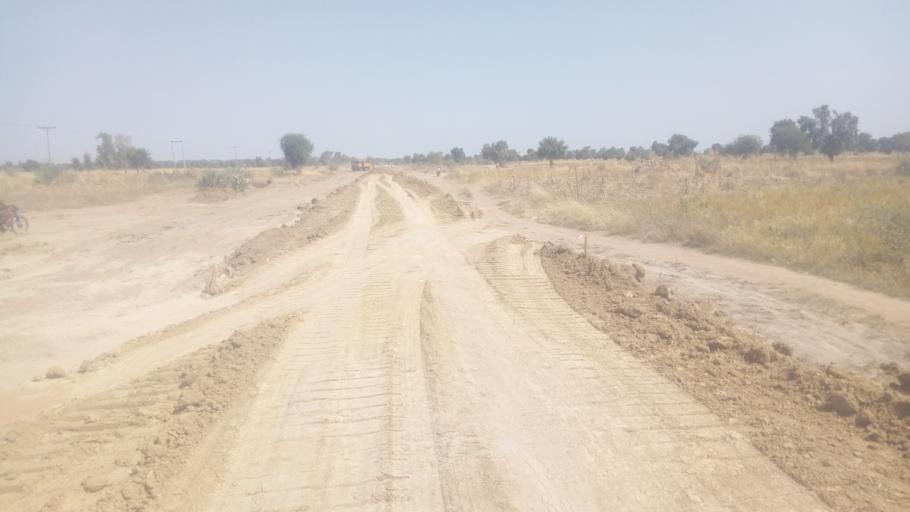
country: NG
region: Adamawa
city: Yola
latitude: 9.1557
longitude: 12.8684
